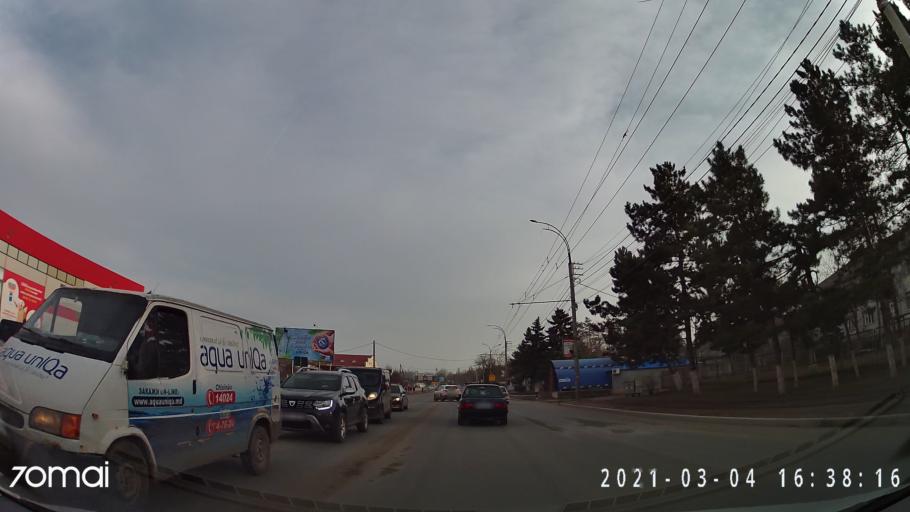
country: MD
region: Balti
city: Balti
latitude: 47.7817
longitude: 27.8903
